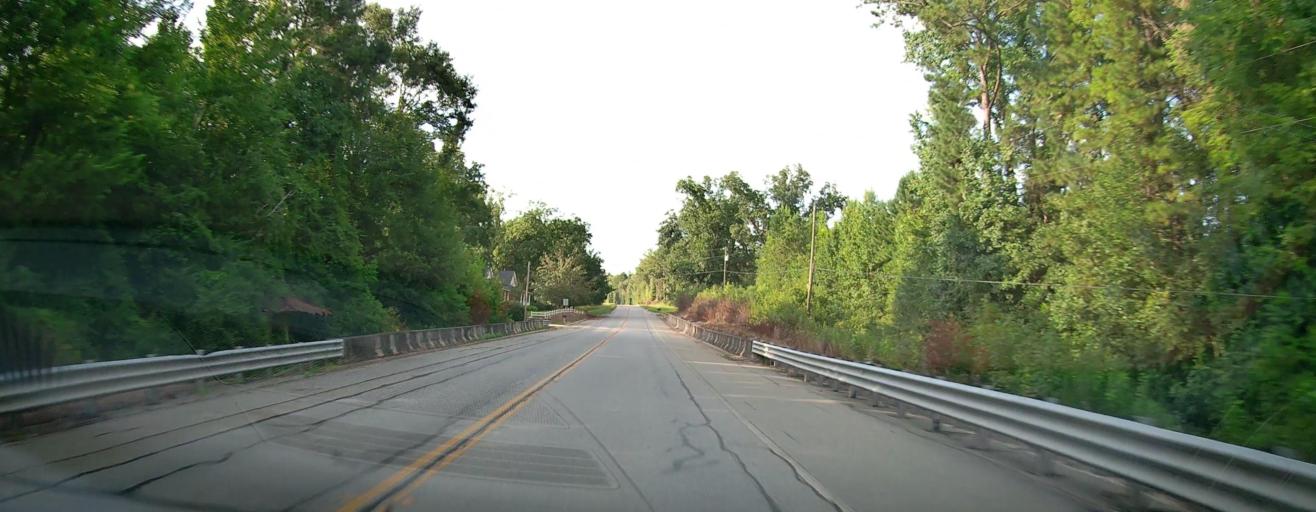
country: US
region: Georgia
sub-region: Crawford County
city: Knoxville
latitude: 32.8661
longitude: -83.9946
